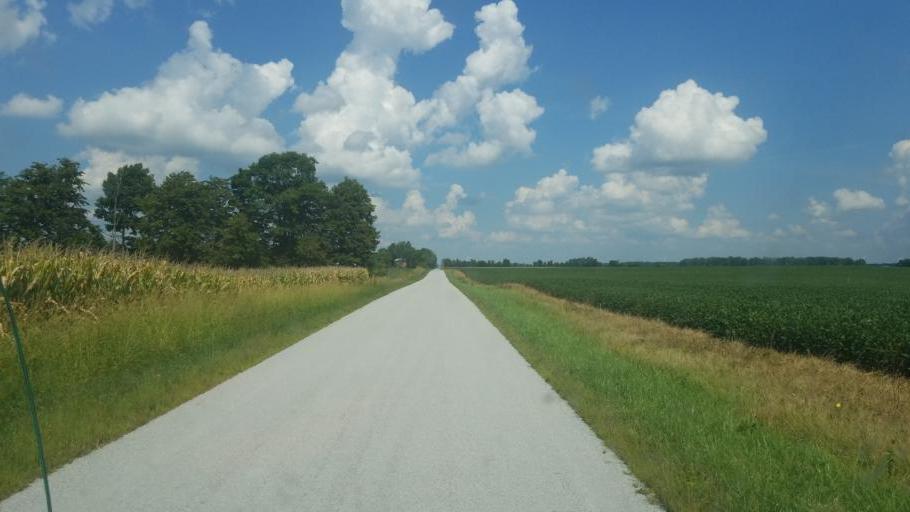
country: US
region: Ohio
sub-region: Hardin County
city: Ada
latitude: 40.7353
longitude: -83.7098
